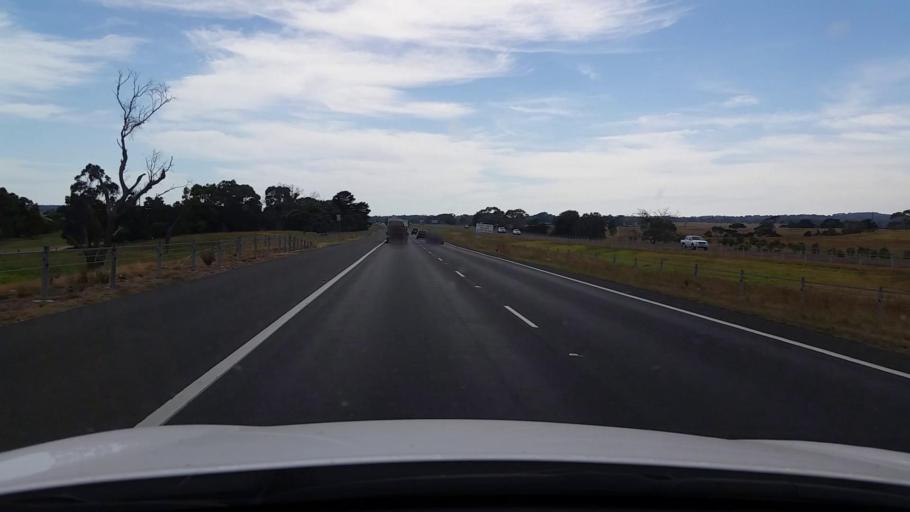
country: AU
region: Victoria
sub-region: Mornington Peninsula
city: Safety Beach
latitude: -38.3256
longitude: 144.9971
